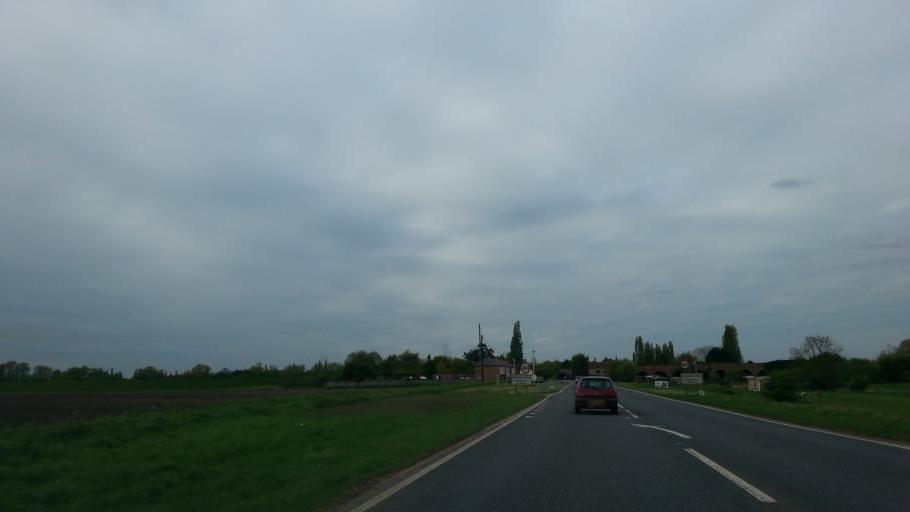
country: GB
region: England
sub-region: Cambridgeshire
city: March
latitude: 52.6000
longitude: 0.0624
